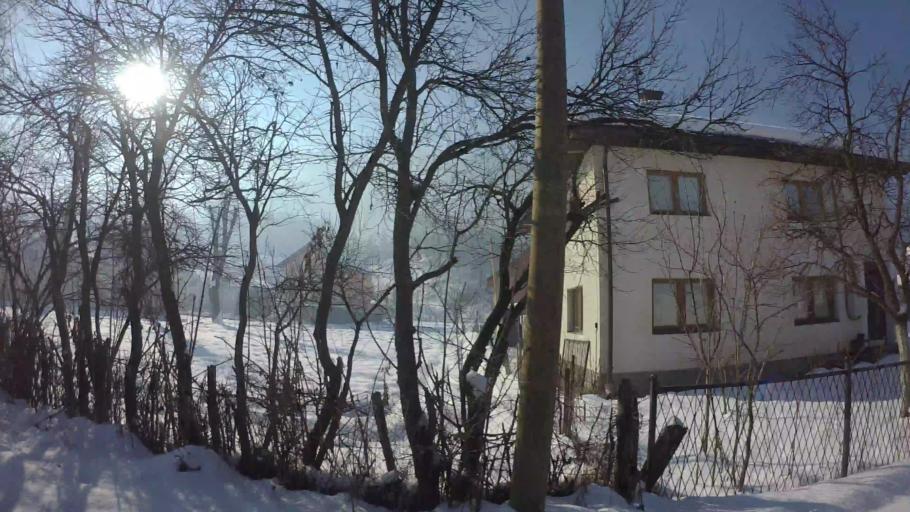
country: BA
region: Federation of Bosnia and Herzegovina
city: Gracanica
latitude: 43.8034
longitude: 18.2999
